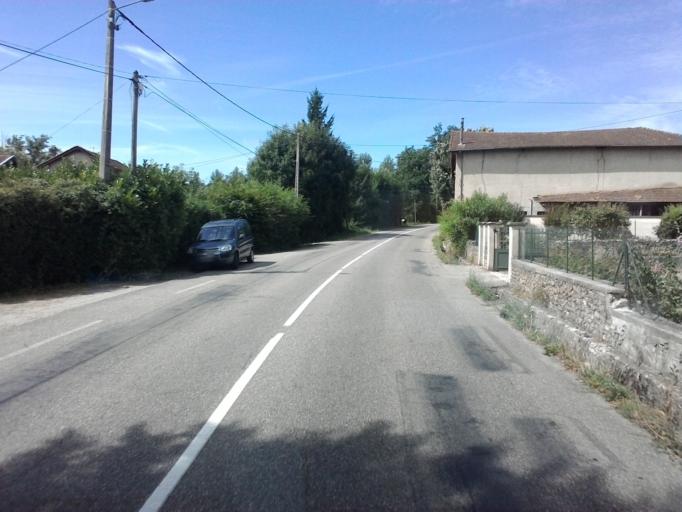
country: FR
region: Rhone-Alpes
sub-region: Departement de l'Isere
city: Le Pin
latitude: 45.4512
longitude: 5.5203
